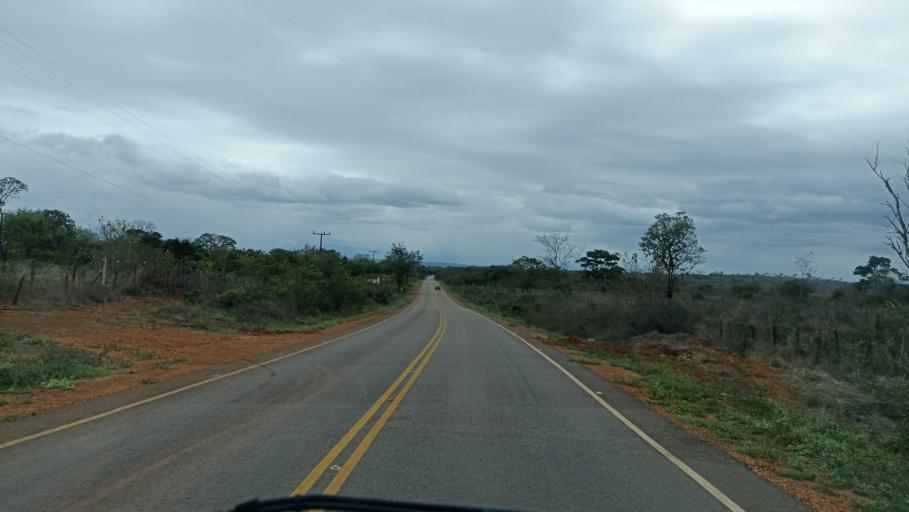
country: BR
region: Bahia
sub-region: Andarai
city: Vera Cruz
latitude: -12.9851
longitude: -41.0089
